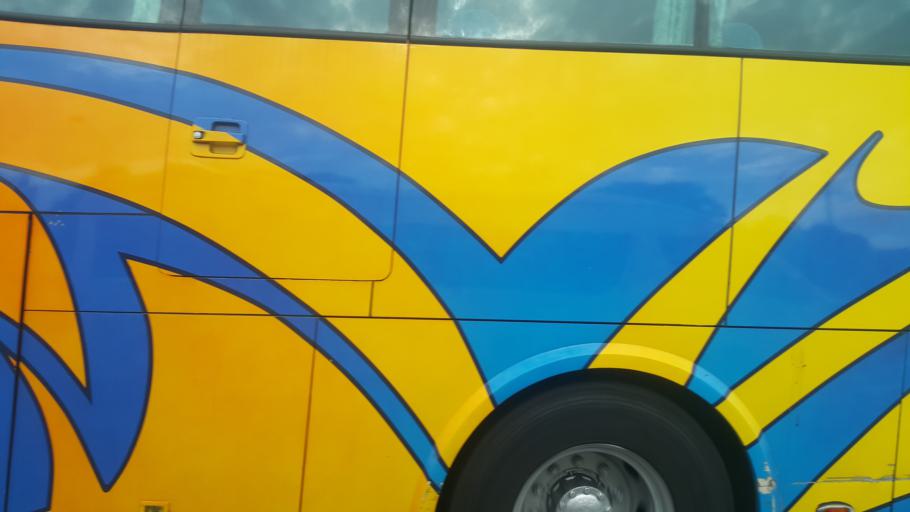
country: MY
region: Johor
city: Pekan Nenas
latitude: 1.4279
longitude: 103.6034
